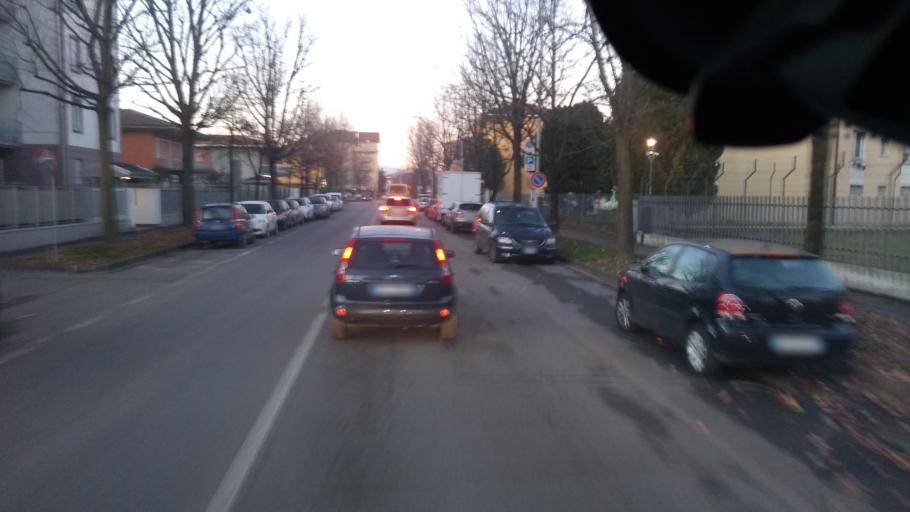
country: IT
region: Lombardy
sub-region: Provincia di Bergamo
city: Treviglio
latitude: 45.5234
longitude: 9.5995
